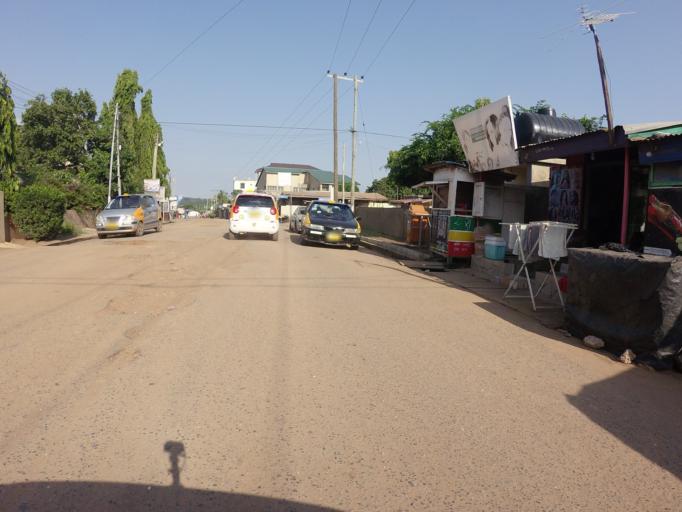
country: GH
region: Greater Accra
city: Dome
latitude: 5.6132
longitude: -0.2376
